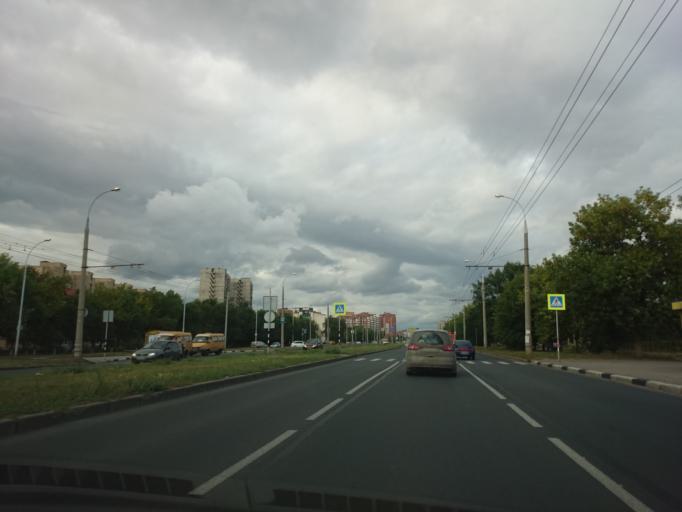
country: RU
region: Samara
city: Tol'yatti
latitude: 53.5083
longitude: 49.3028
